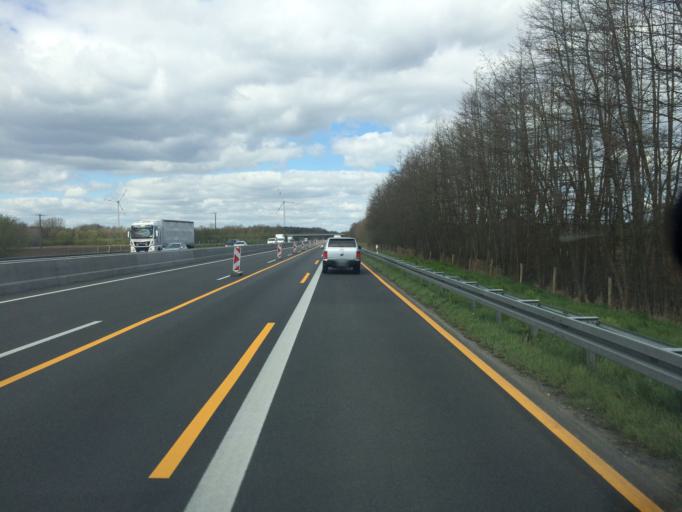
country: DE
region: North Rhine-Westphalia
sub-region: Regierungsbezirk Munster
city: Gescher
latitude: 51.9591
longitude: 7.0468
